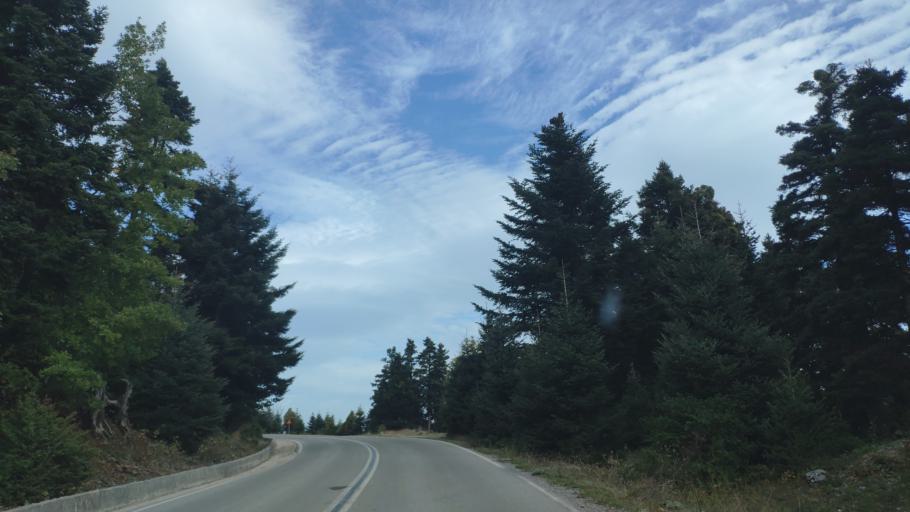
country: GR
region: Central Greece
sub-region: Nomos Fokidos
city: Amfissa
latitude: 38.6503
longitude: 22.3845
